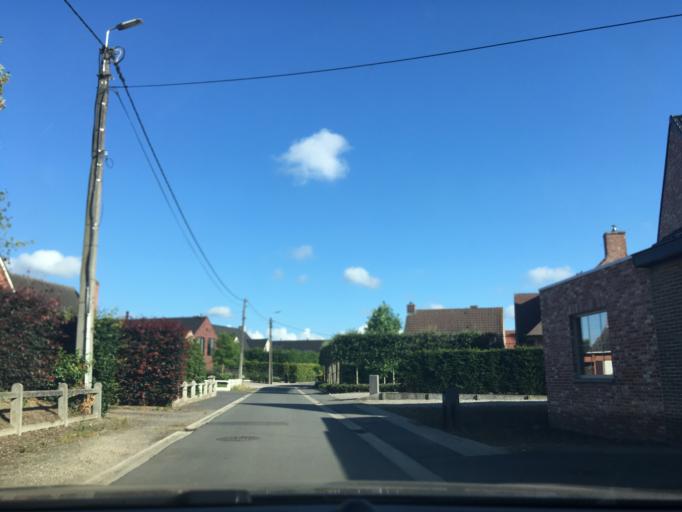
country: BE
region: Flanders
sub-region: Provincie West-Vlaanderen
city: Ardooie
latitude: 50.9696
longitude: 3.2141
